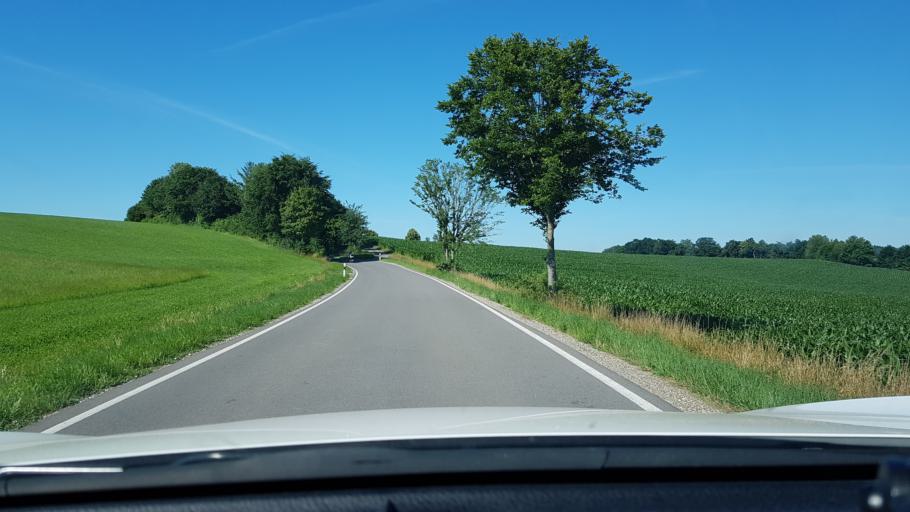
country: DE
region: Baden-Wuerttemberg
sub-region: Tuebingen Region
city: Gutenzell-Hurbel
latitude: 48.1165
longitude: 9.9554
